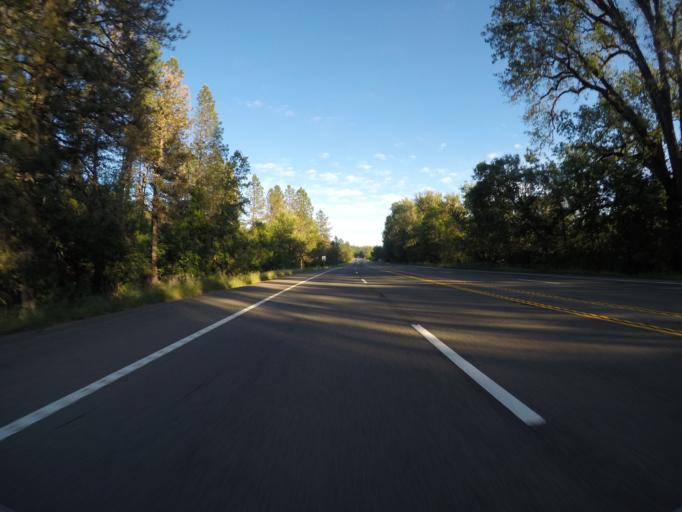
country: US
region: California
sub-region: Mendocino County
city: Laytonville
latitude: 39.7266
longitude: -123.5042
